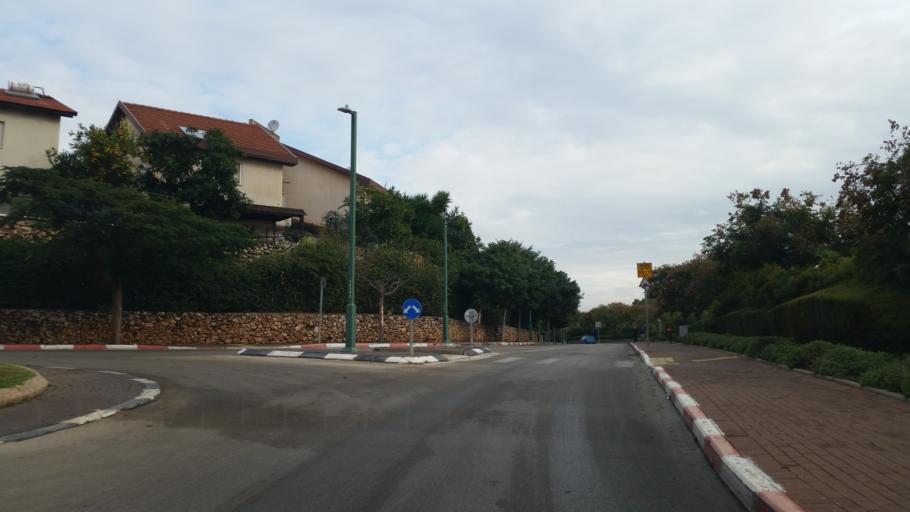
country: IL
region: Tel Aviv
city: Ramat HaSharon
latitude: 32.1498
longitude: 34.8484
